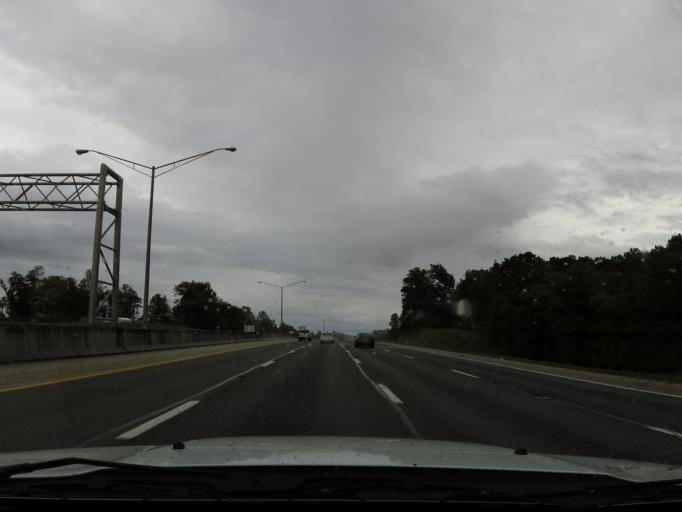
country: US
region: Kentucky
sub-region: Laurel County
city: London
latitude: 37.1190
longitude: -84.1053
